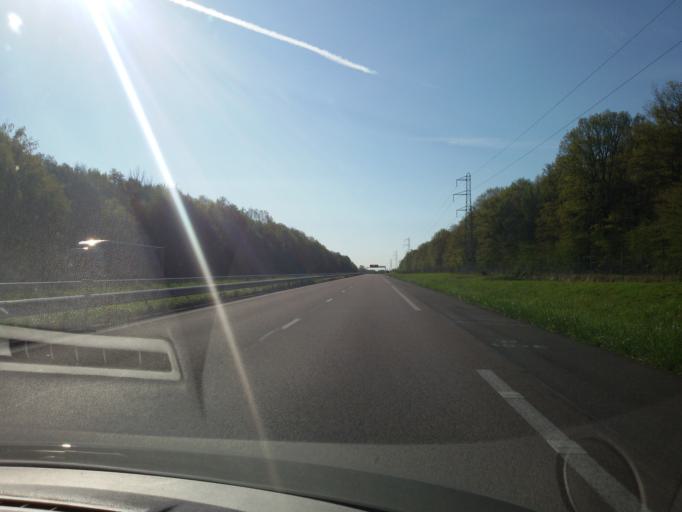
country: FR
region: Centre
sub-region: Departement du Loiret
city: Courtenay
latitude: 48.0755
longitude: 3.0637
